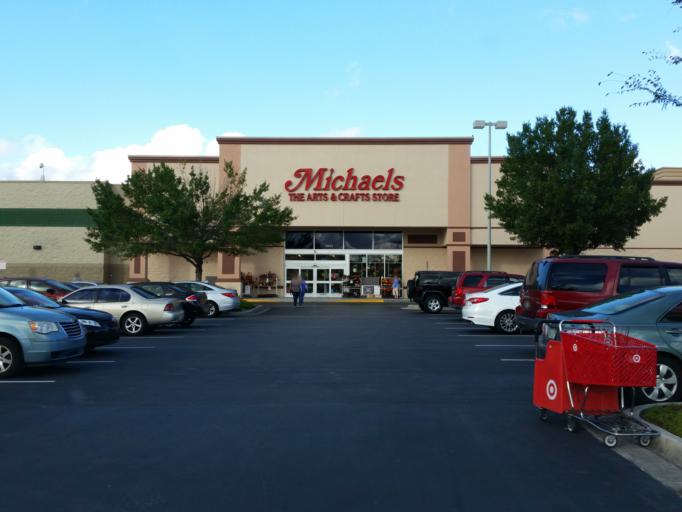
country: US
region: Florida
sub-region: Hillsborough County
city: Town 'n' Country
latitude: 28.0161
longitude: -82.6141
